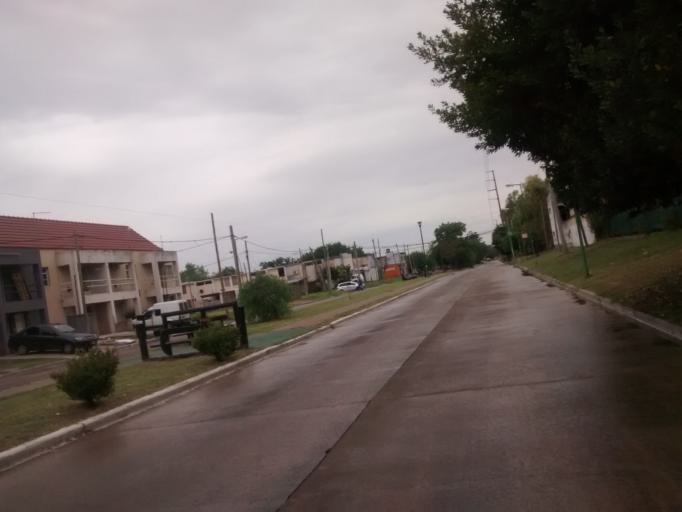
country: AR
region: Buenos Aires
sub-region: Partido de La Plata
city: La Plata
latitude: -34.9055
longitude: -57.9866
